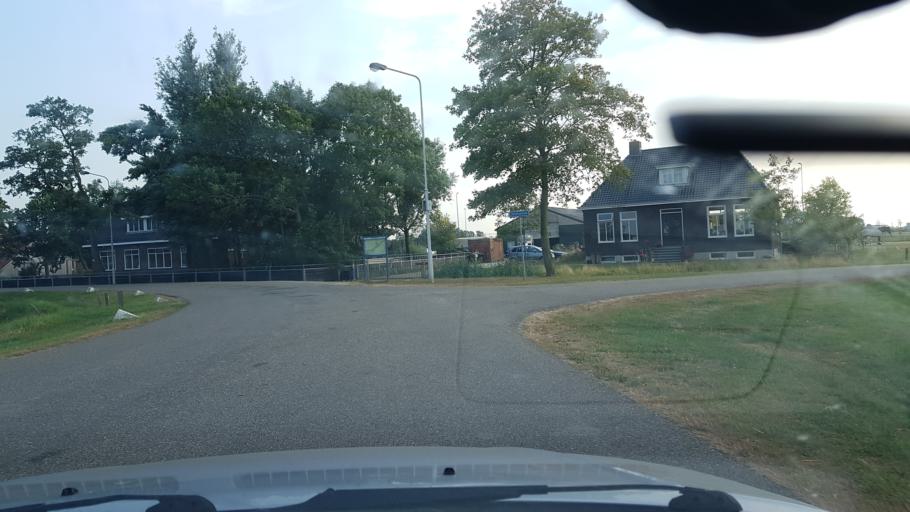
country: NL
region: Friesland
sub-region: Gemeente Ferwerderadiel
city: Burdaard
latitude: 53.2990
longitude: 5.8771
